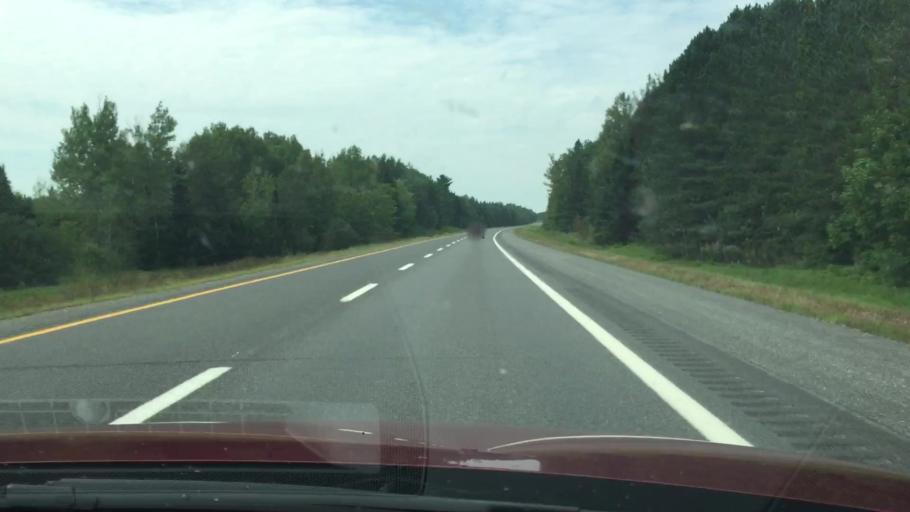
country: US
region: Maine
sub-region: Aroostook County
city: Houlton
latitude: 46.1378
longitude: -67.9117
